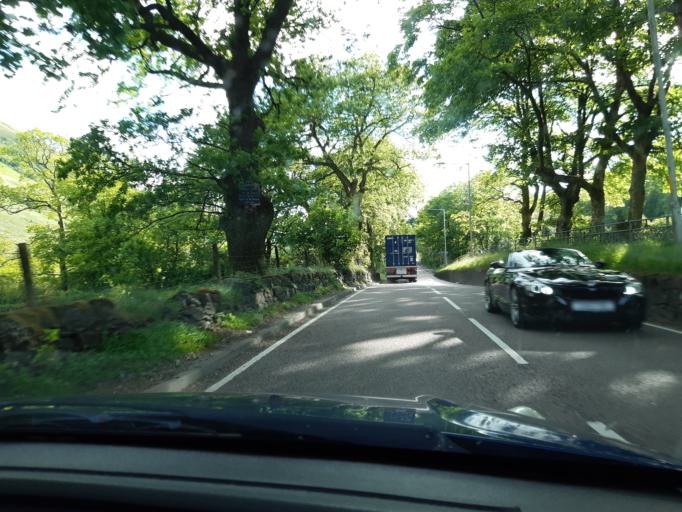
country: GB
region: Scotland
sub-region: Argyll and Bute
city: Garelochhead
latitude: 56.2020
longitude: -4.7239
